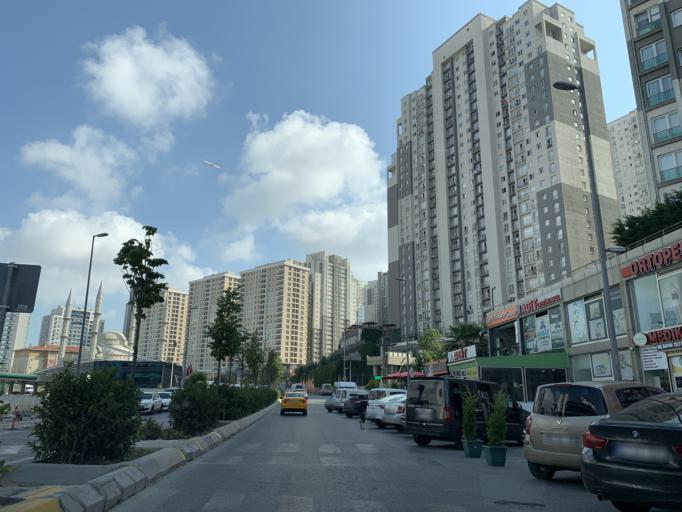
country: TR
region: Istanbul
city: Esenyurt
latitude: 41.0260
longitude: 28.6590
